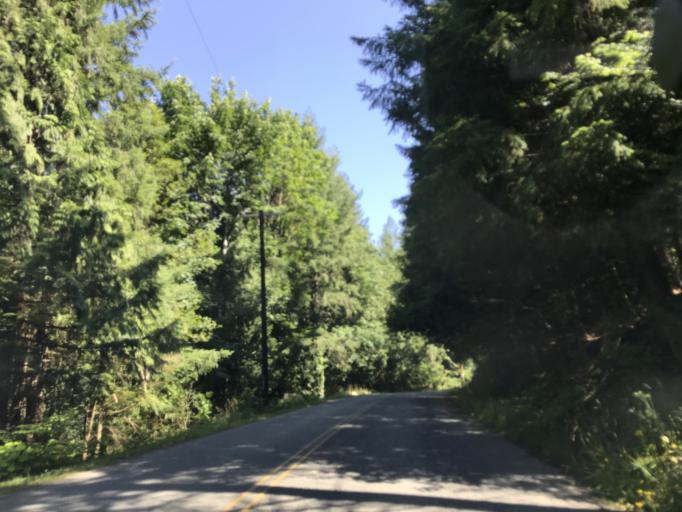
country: US
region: Washington
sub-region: King County
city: Hobart
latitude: 47.3755
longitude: -121.8749
